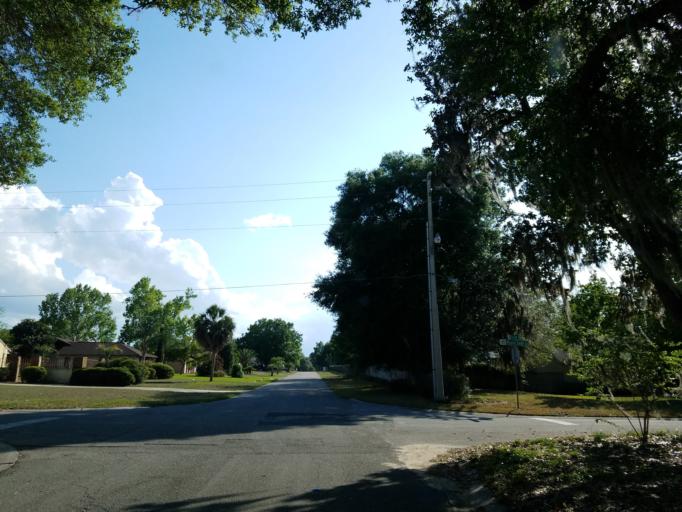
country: US
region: Florida
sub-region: Lake County
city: Fruitland Park
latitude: 28.8619
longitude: -81.8665
